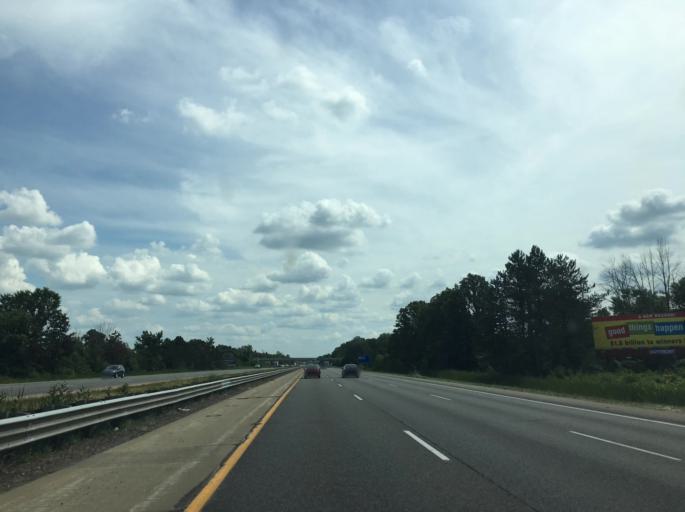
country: US
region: Michigan
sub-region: Genesee County
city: Beecher
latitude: 43.0794
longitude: -83.7629
